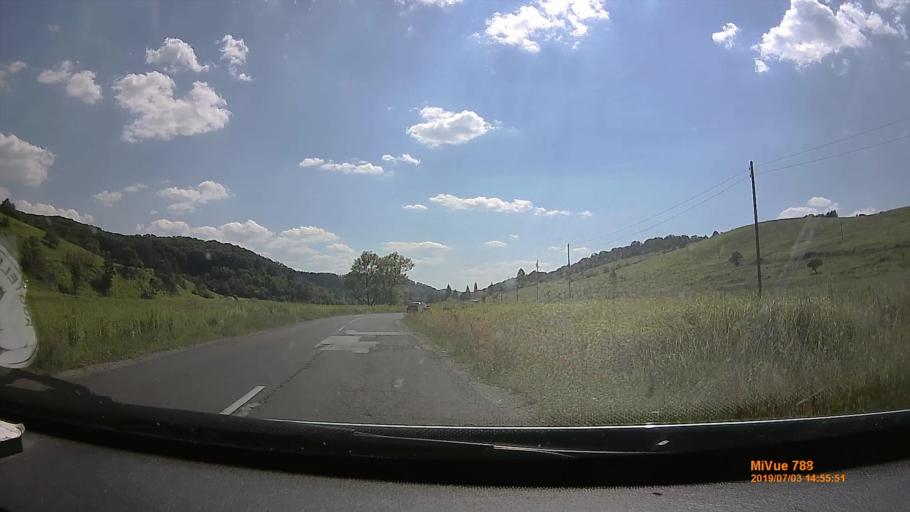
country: HU
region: Borsod-Abauj-Zemplen
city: Putnok
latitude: 48.2601
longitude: 20.3981
